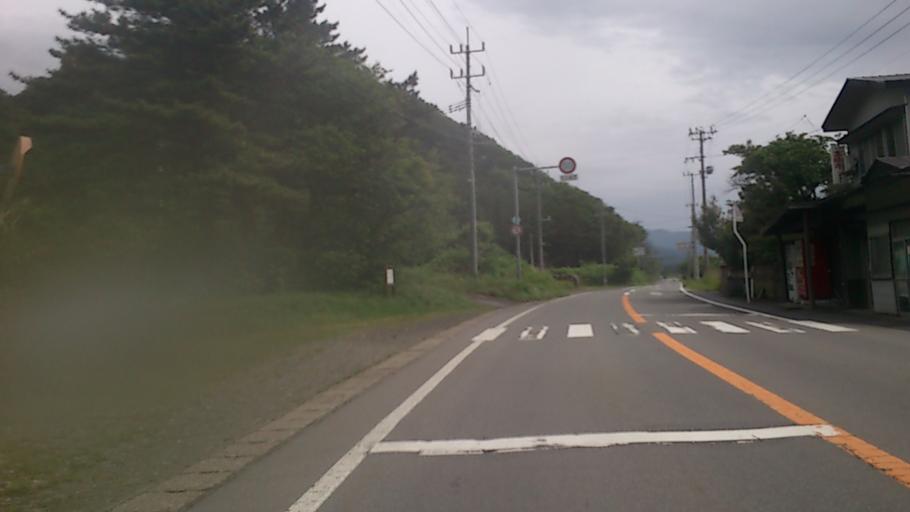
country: JP
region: Akita
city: Noshiromachi
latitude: 40.5356
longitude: 139.9475
